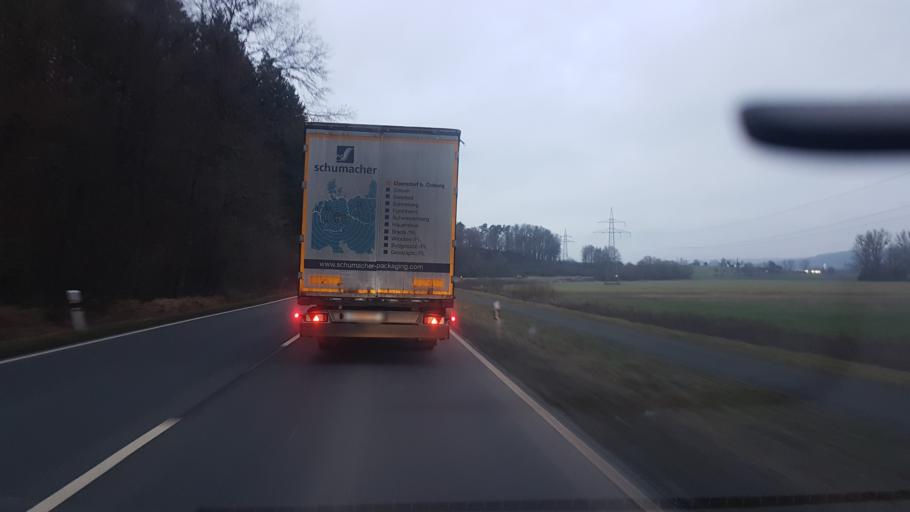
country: DE
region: Bavaria
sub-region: Regierungsbezirk Unterfranken
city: Rentweinsdorf
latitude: 50.0715
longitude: 10.7944
